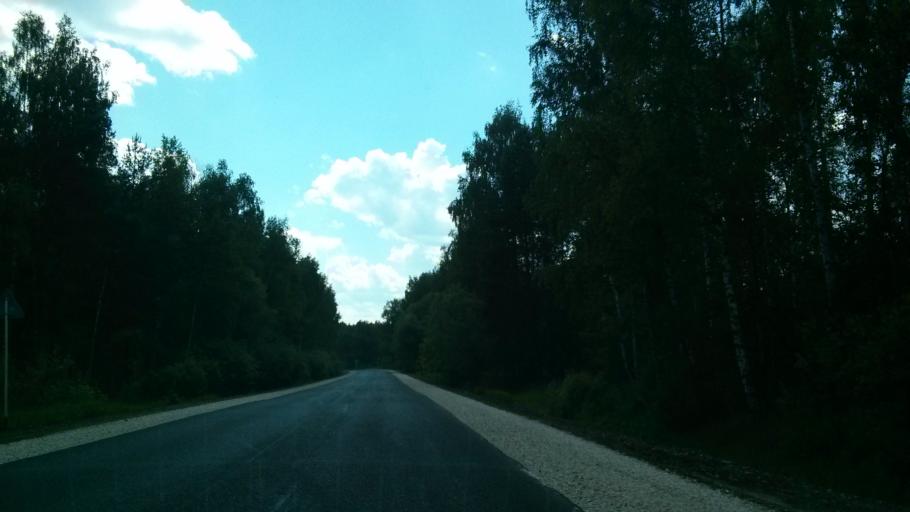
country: RU
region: Vladimir
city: Murom
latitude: 55.5069
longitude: 41.9173
